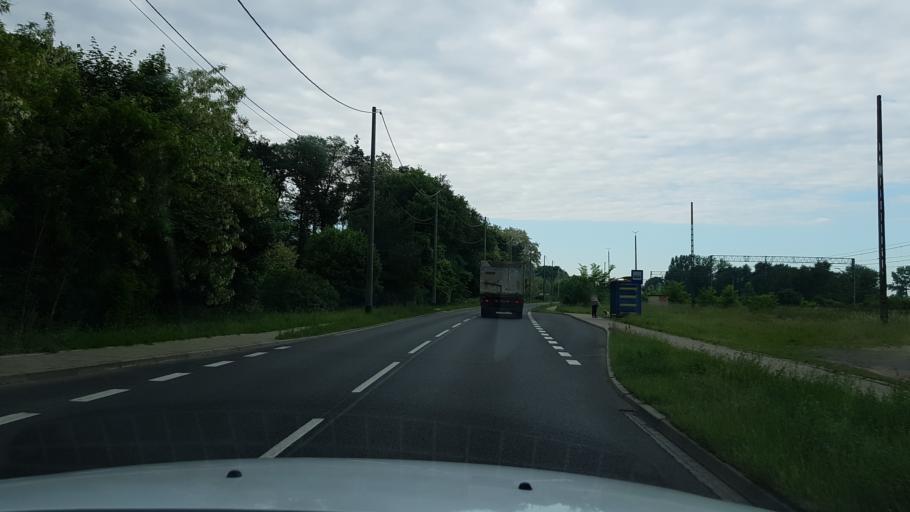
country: PL
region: West Pomeranian Voivodeship
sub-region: Powiat gryfinski
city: Gryfino
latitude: 53.3058
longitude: 14.5294
